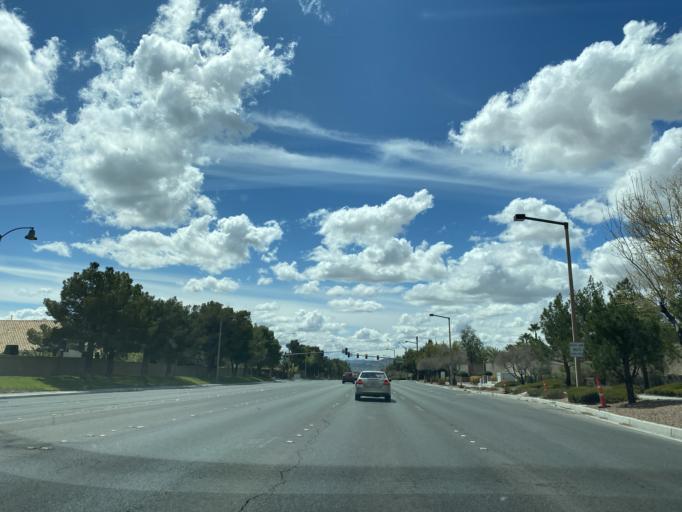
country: US
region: Nevada
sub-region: Clark County
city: Summerlin South
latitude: 36.1385
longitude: -115.3154
